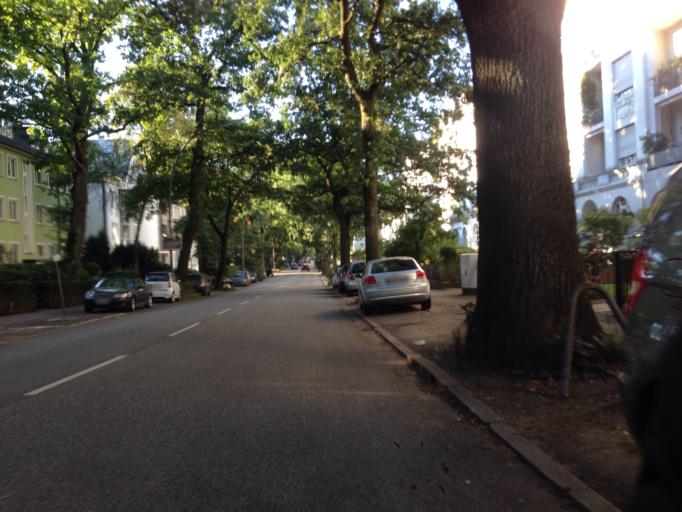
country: DE
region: Hamburg
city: Hamburg
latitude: 53.5836
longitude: 10.0055
